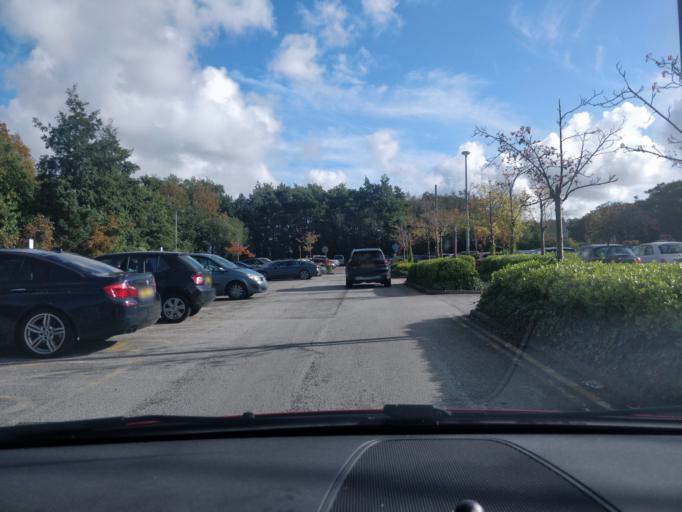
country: GB
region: England
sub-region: Lancashire
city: Ormskirk
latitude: 53.5642
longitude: -2.8698
